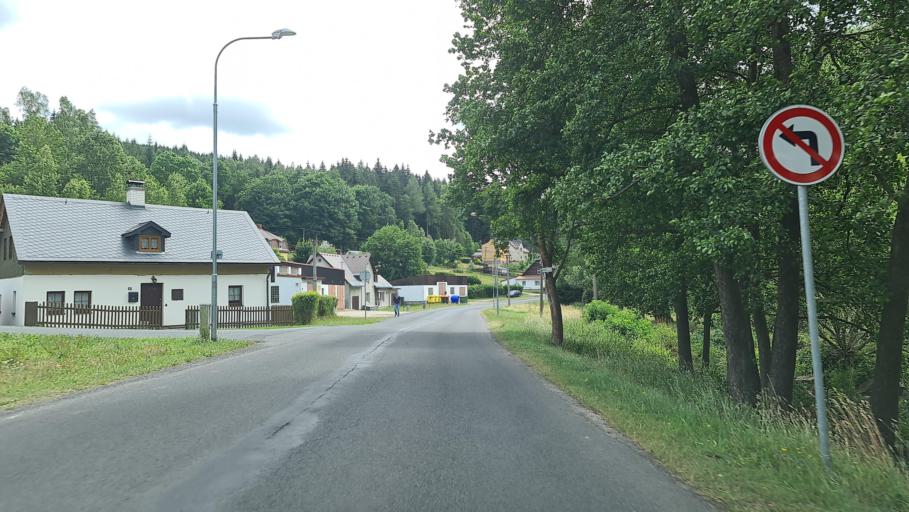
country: CZ
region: Karlovarsky
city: Kraslice
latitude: 50.3558
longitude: 12.5272
